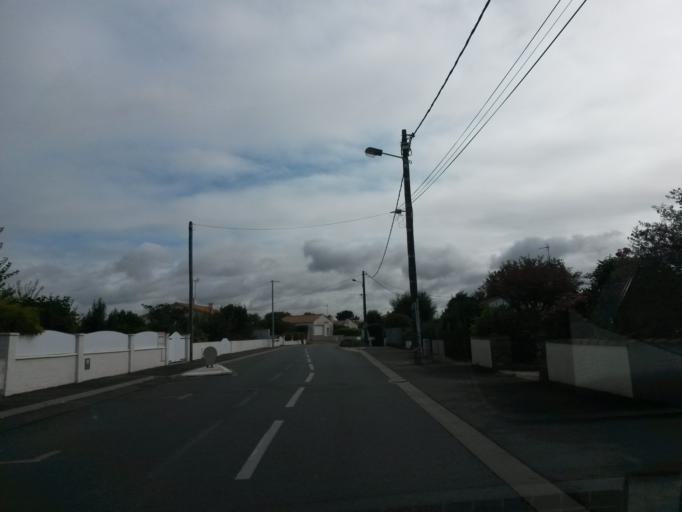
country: FR
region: Pays de la Loire
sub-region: Departement de la Vendee
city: Olonne-sur-Mer
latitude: 46.5234
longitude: -1.7820
